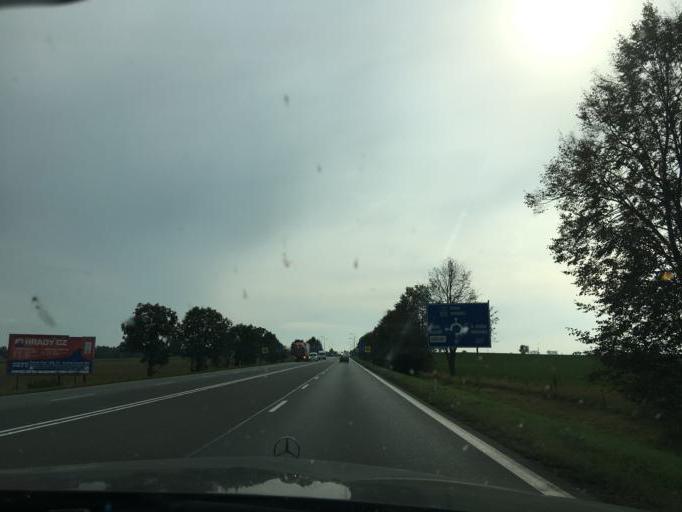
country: CZ
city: Stezery
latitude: 50.2135
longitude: 15.7846
